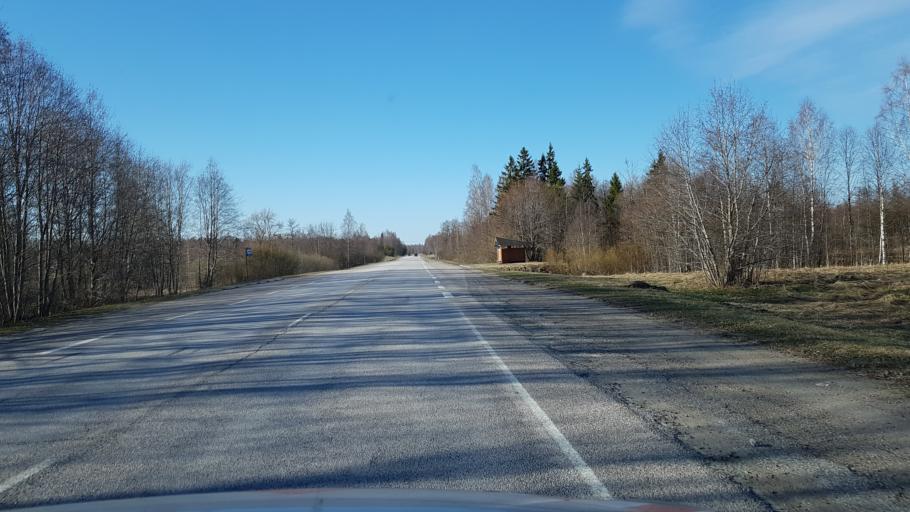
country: EE
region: Ida-Virumaa
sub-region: Johvi vald
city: Johvi
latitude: 59.1736
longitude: 27.3504
